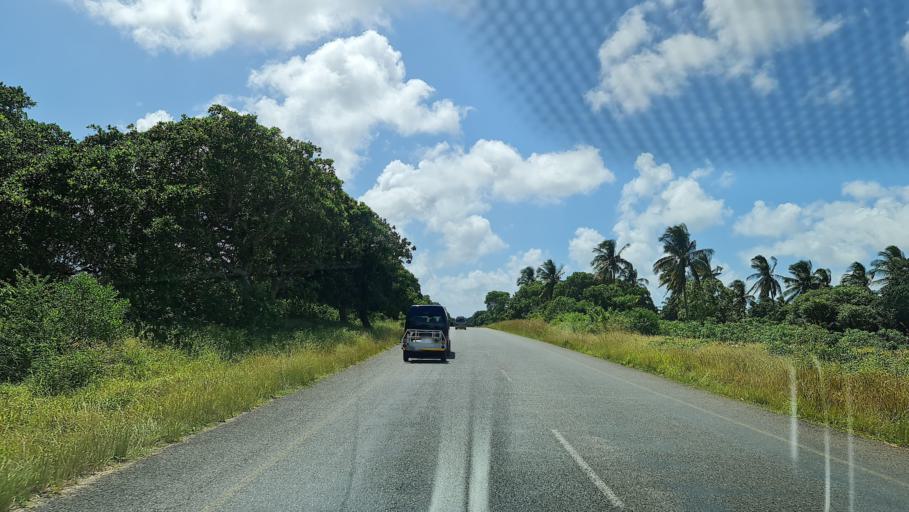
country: MZ
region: Inhambane
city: Maxixe
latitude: -24.5406
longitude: 34.9233
